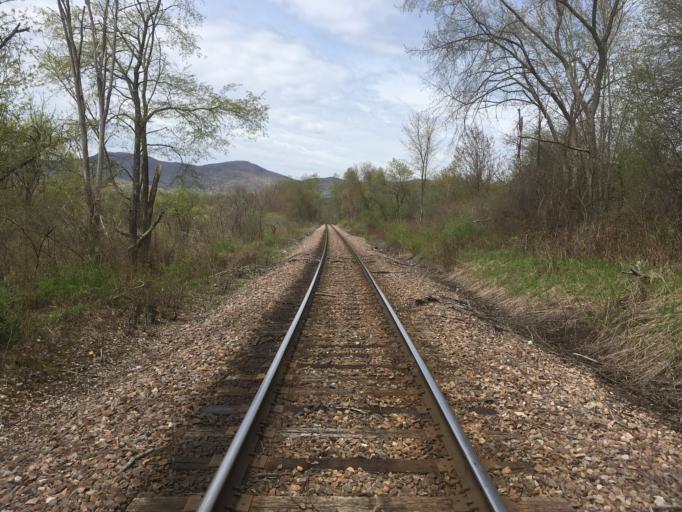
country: US
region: Vermont
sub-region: Rutland County
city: Brandon
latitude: 43.7149
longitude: -73.0441
